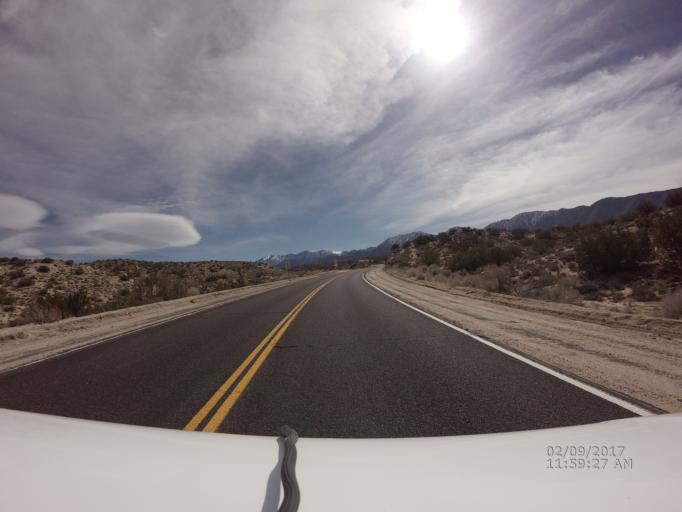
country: US
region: California
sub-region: Los Angeles County
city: Littlerock
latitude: 34.4745
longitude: -117.9006
